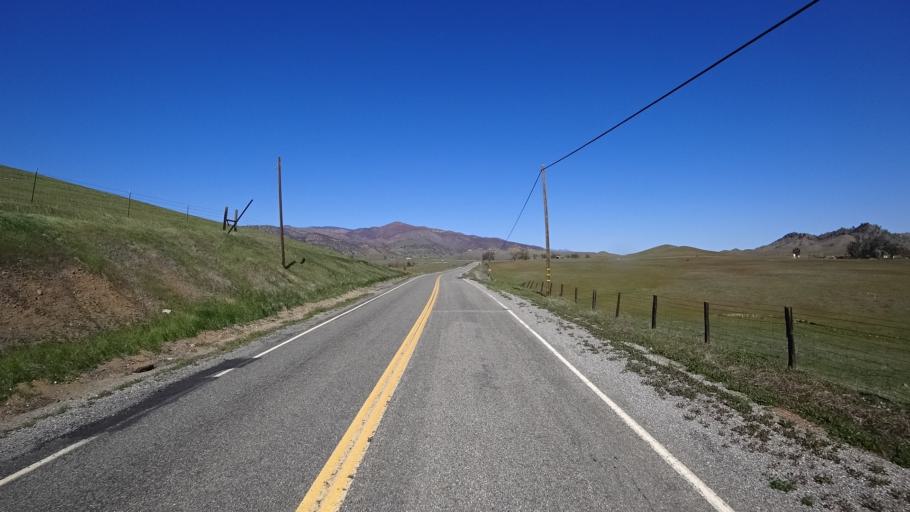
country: US
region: California
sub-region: Glenn County
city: Orland
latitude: 39.6907
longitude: -122.5459
